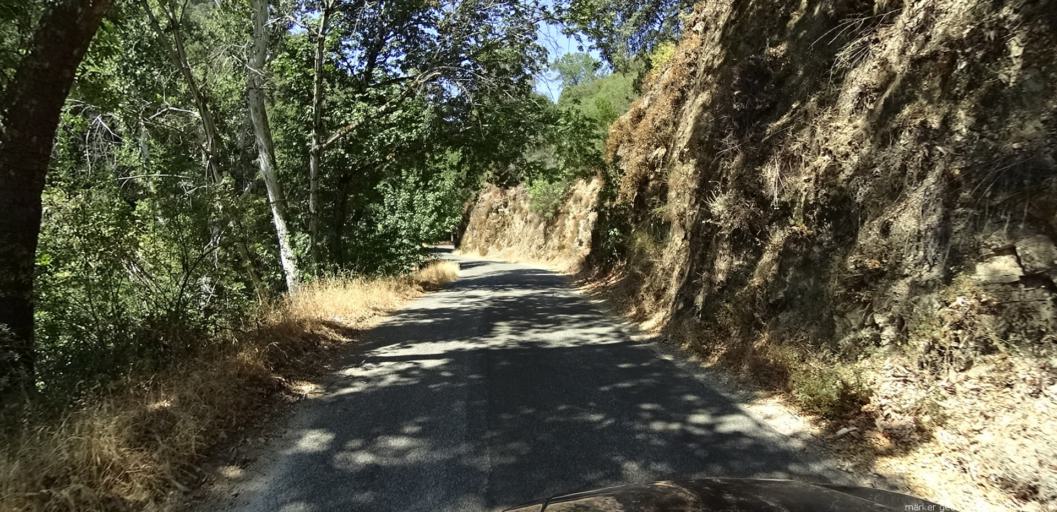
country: US
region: California
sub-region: Monterey County
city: King City
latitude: 36.0133
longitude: -121.4137
